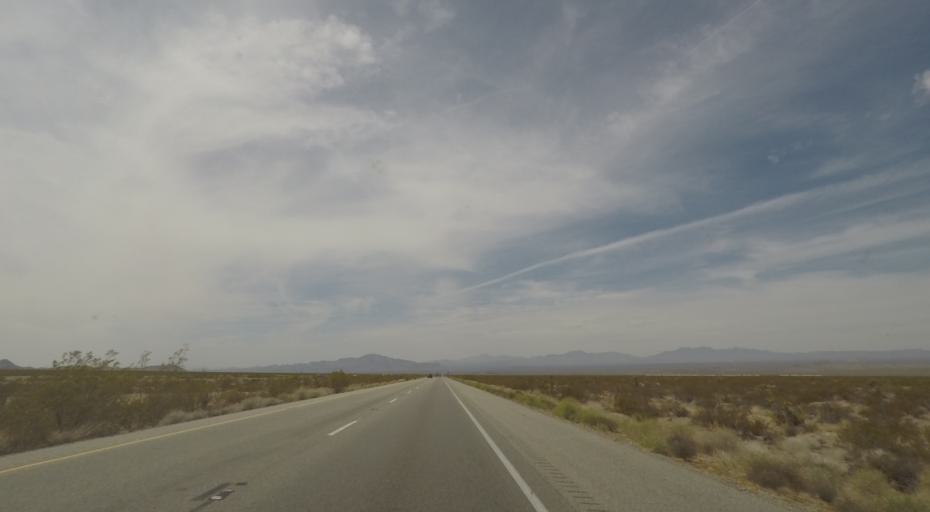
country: US
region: California
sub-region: San Bernardino County
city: Needles
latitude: 34.8255
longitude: -115.0860
